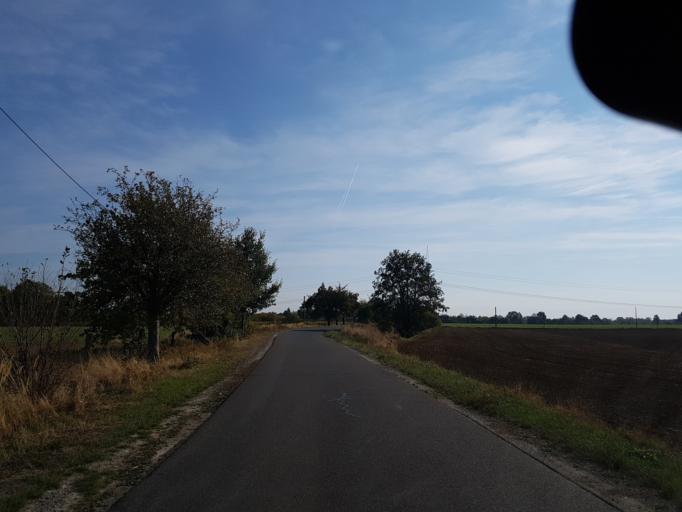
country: DE
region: Brandenburg
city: Doberlug-Kirchhain
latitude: 51.6463
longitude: 13.5452
